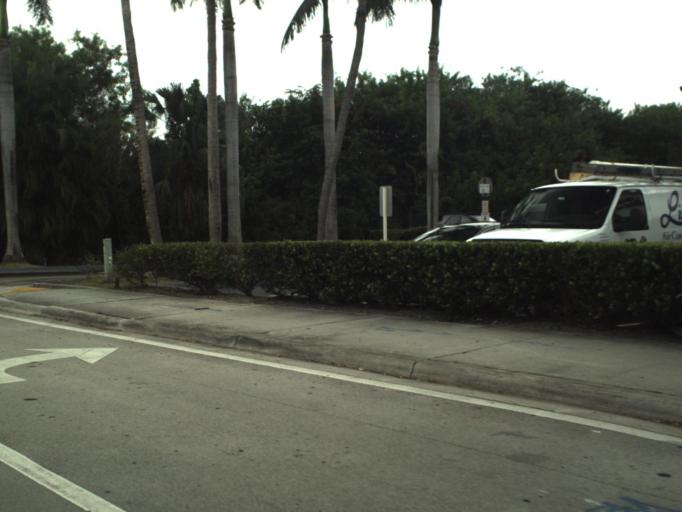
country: US
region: Florida
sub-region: Broward County
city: Dania Beach
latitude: 26.0481
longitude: -80.1582
